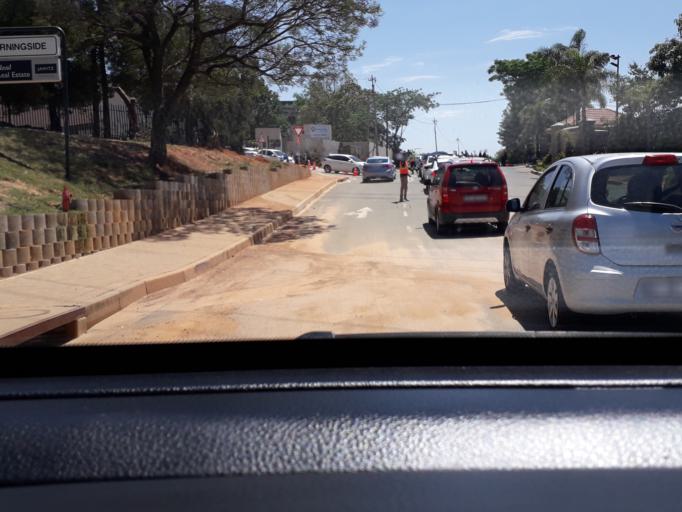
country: ZA
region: Gauteng
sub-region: City of Johannesburg Metropolitan Municipality
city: Modderfontein
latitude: -26.0903
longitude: 28.0633
